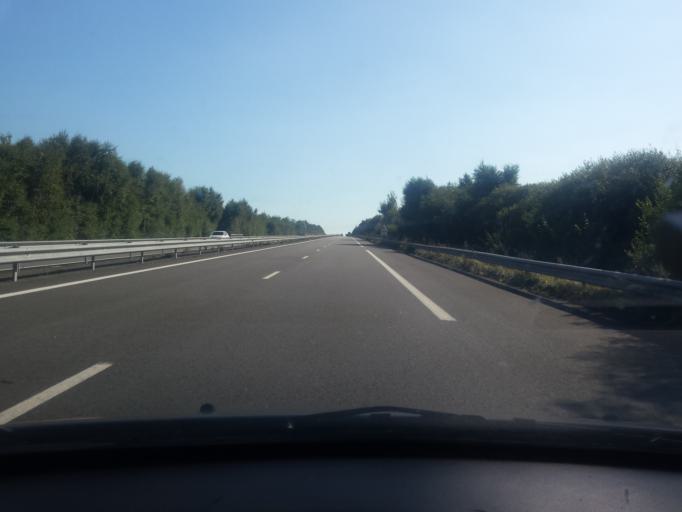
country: FR
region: Brittany
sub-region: Departement du Morbihan
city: Naizin
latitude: 47.9779
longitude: -2.8694
